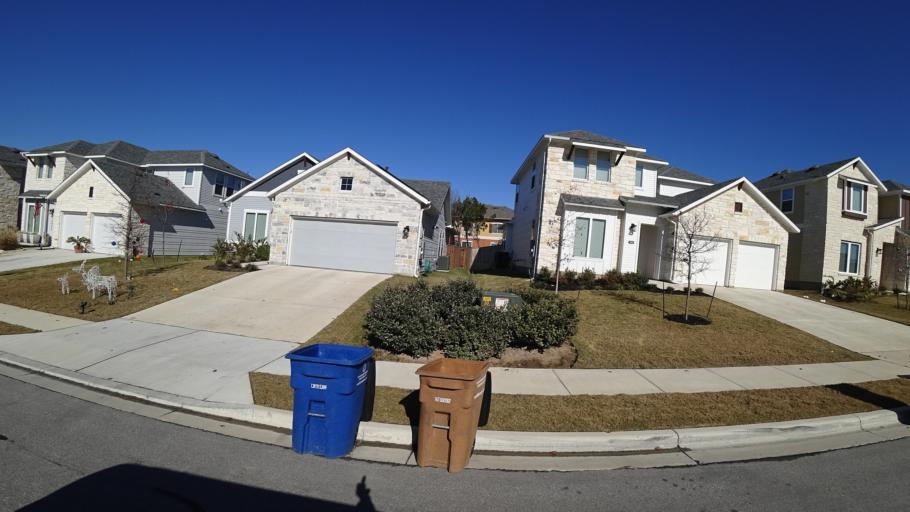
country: US
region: Texas
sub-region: Travis County
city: Wells Branch
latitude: 30.4277
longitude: -97.6986
